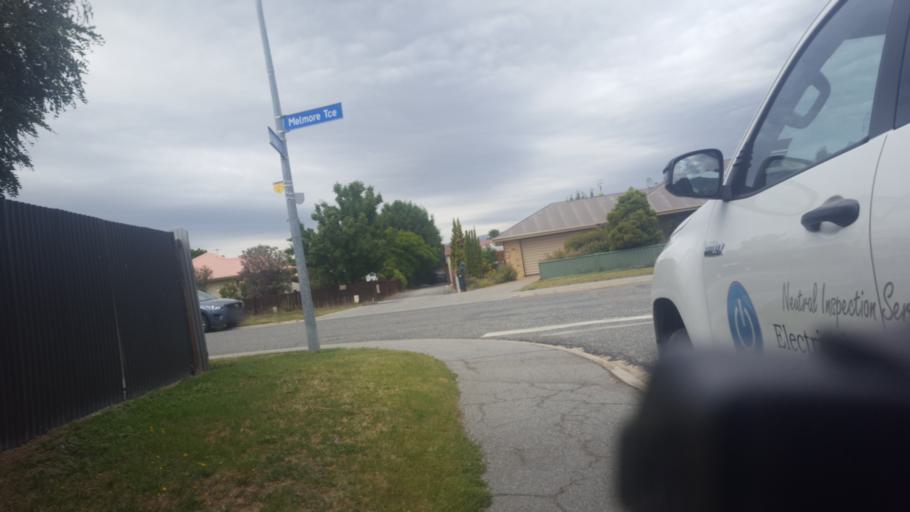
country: NZ
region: Otago
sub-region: Queenstown-Lakes District
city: Wanaka
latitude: -45.0468
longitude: 169.1977
